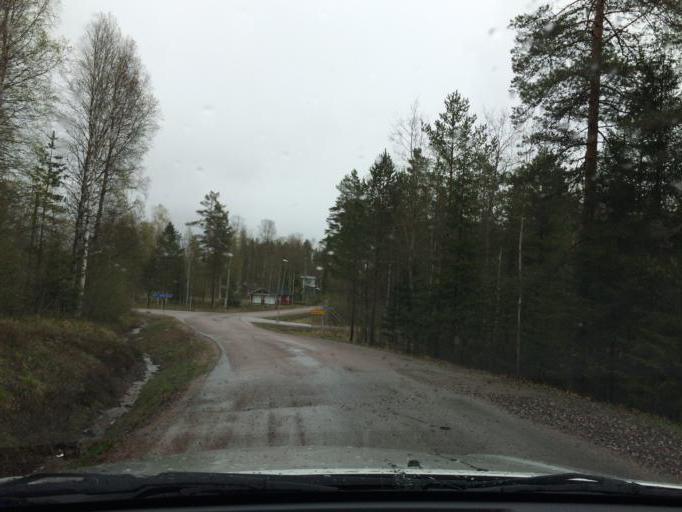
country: SE
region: Dalarna
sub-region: Ludvika Kommun
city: Abborrberget
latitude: 60.0432
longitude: 14.7306
